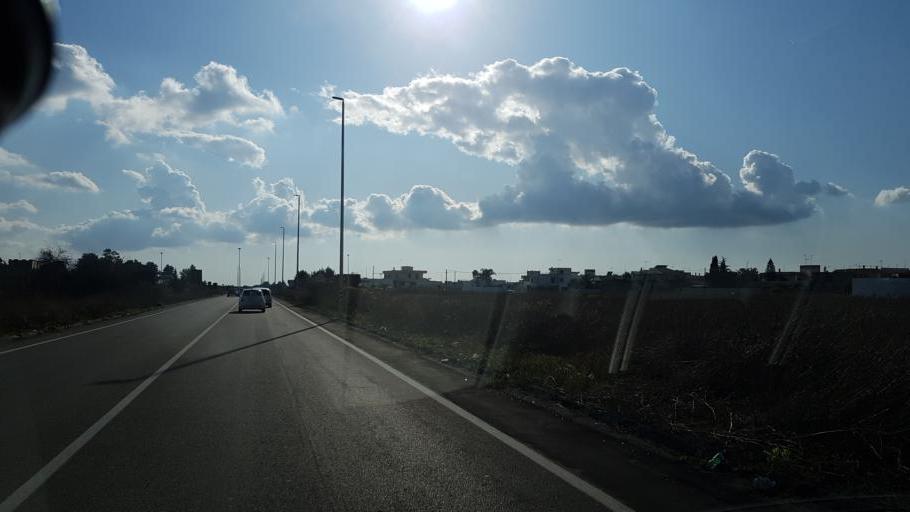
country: IT
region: Apulia
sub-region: Provincia di Lecce
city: Salice Salentino
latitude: 40.3828
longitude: 17.9703
